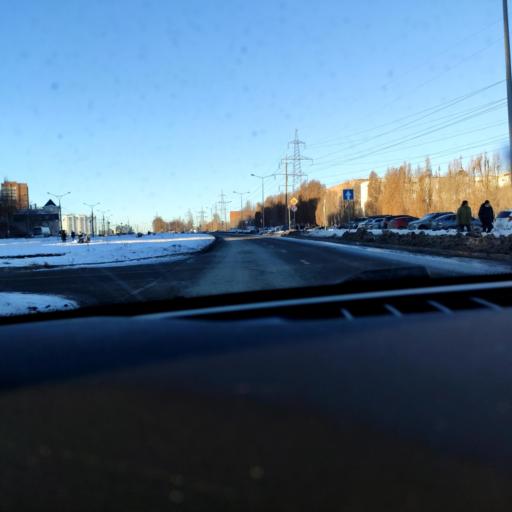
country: RU
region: Samara
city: Samara
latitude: 53.2577
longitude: 50.2478
